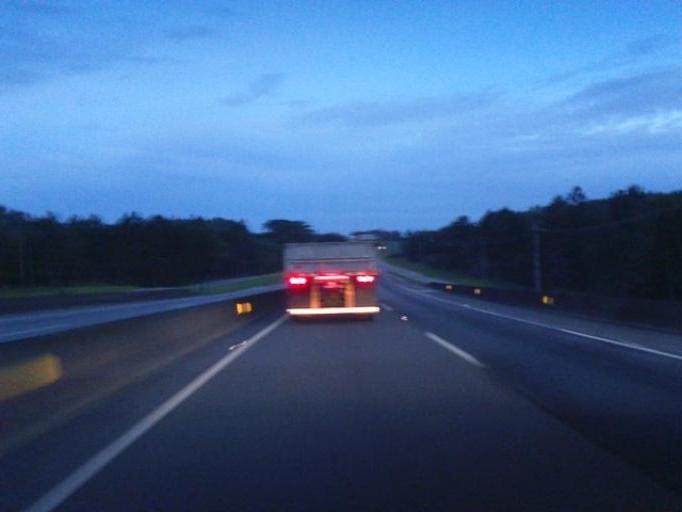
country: BR
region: Santa Catarina
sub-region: Joinville
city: Joinville
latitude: -26.4558
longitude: -48.7638
